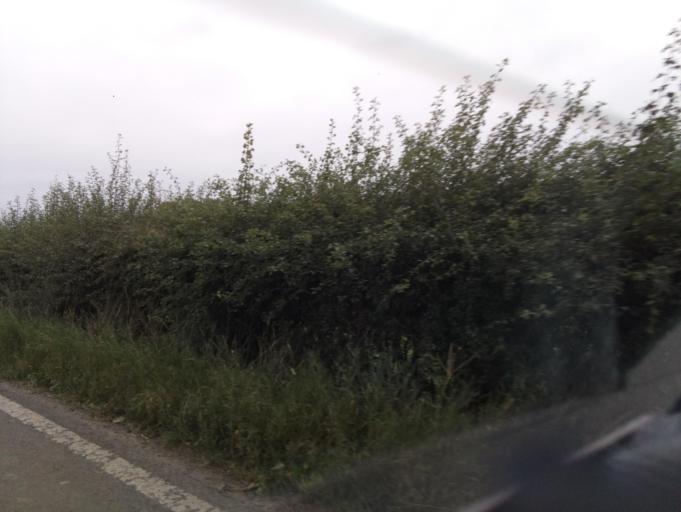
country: GB
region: England
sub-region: Derbyshire
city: Duffield
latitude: 53.0133
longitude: -1.5380
